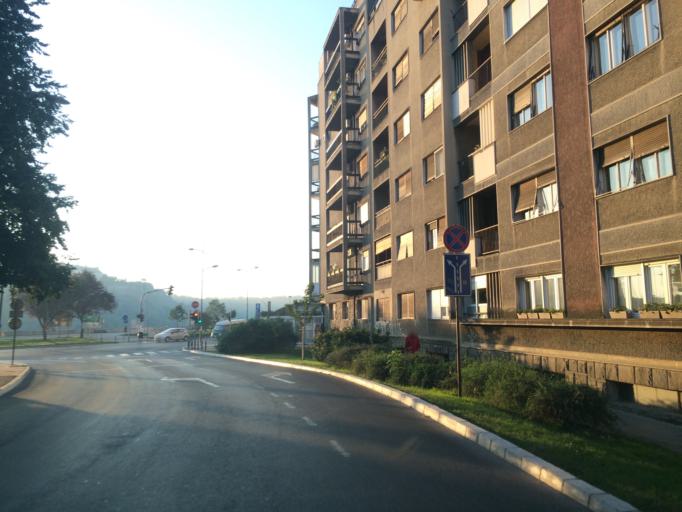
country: RS
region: Autonomna Pokrajina Vojvodina
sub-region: Juznobacki Okrug
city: Novi Sad
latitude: 45.2538
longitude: 19.8545
